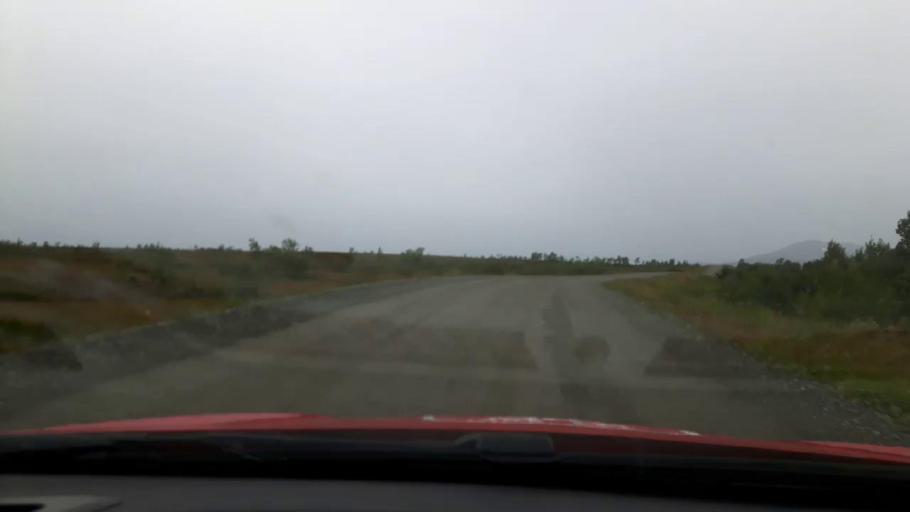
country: NO
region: Nord-Trondelag
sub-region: Meraker
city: Meraker
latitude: 63.6161
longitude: 12.2869
